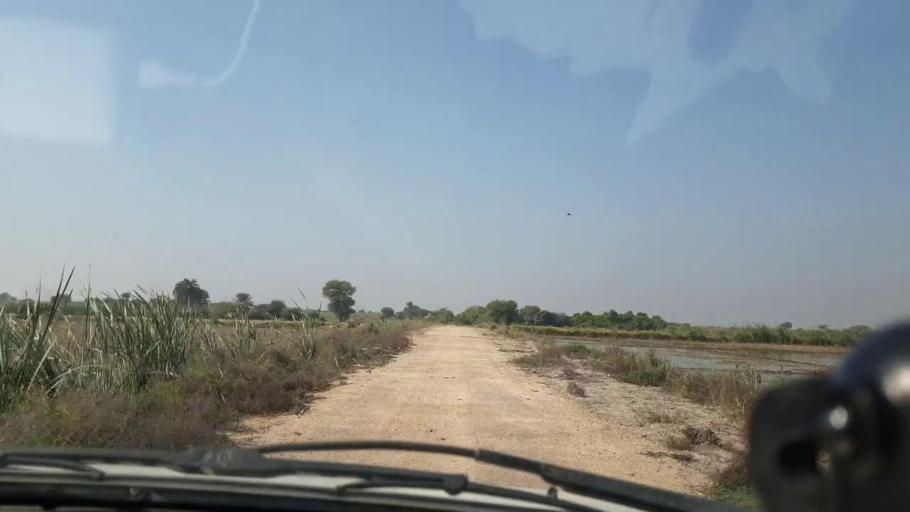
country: PK
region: Sindh
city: Bulri
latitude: 24.8328
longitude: 68.3146
